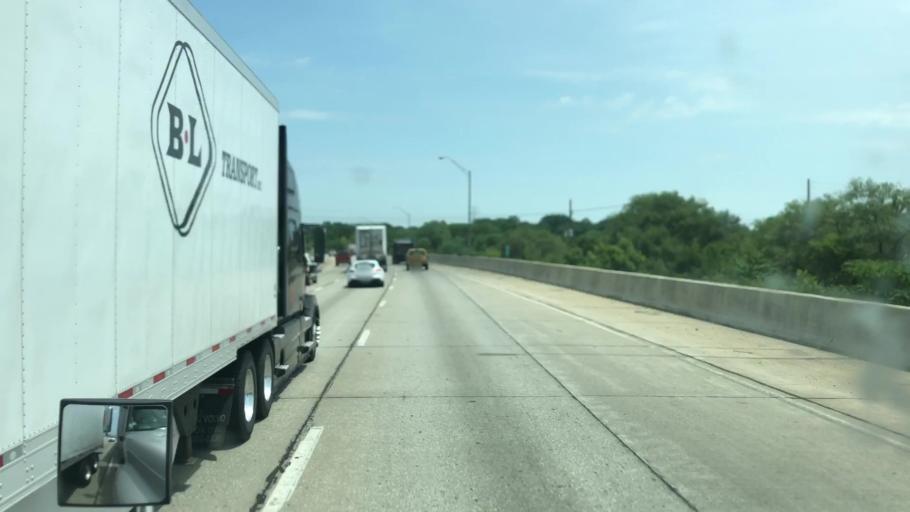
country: US
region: Indiana
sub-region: Marion County
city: Indianapolis
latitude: 39.7530
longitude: -86.2176
